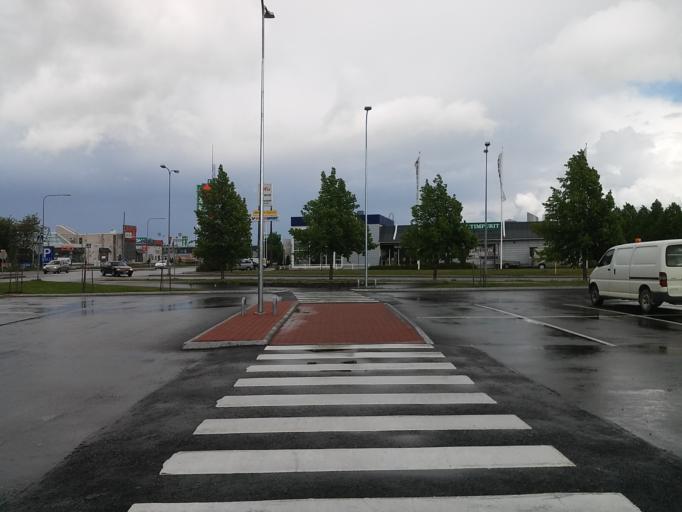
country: FI
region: Varsinais-Suomi
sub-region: Turku
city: Turku
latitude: 60.4724
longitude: 22.2210
